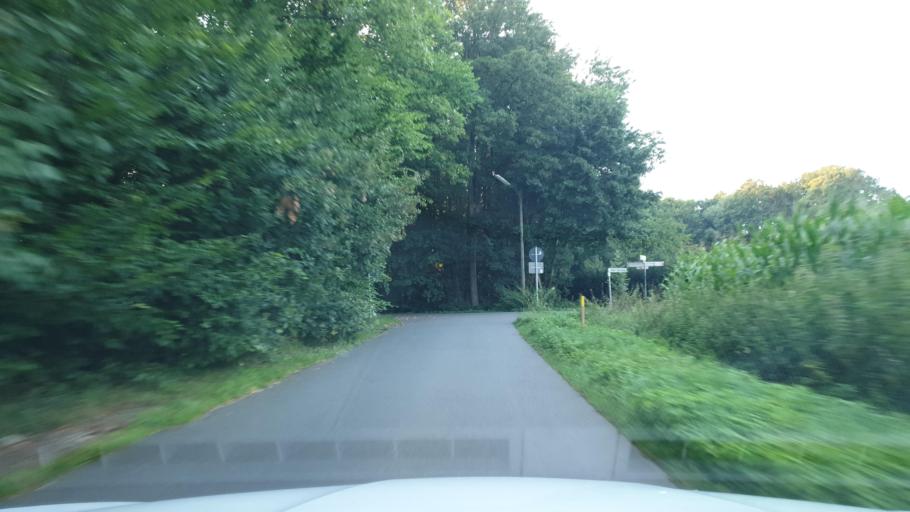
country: DE
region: North Rhine-Westphalia
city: Bad Oeynhausen
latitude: 52.2267
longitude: 8.7516
